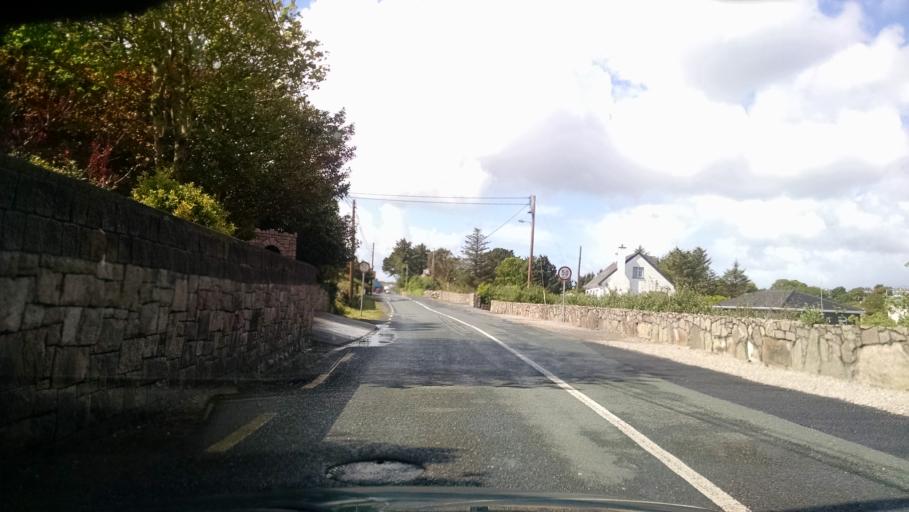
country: IE
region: Connaught
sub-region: County Galway
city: Oughterard
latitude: 53.2664
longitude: -9.5938
